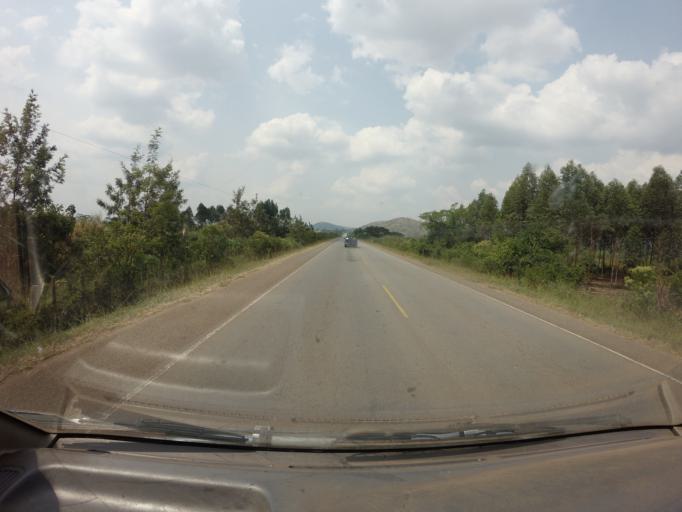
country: UG
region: Central Region
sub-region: Lyantonde District
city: Lyantonde
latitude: -0.3969
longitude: 31.1733
